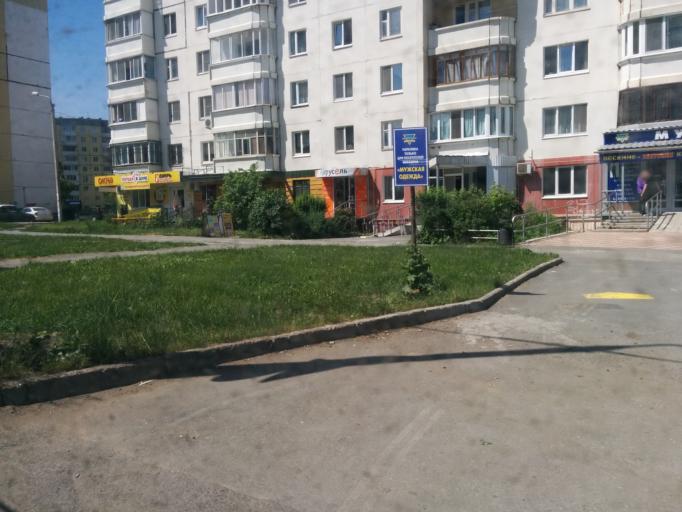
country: RU
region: Perm
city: Perm
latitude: 58.0040
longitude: 56.3056
